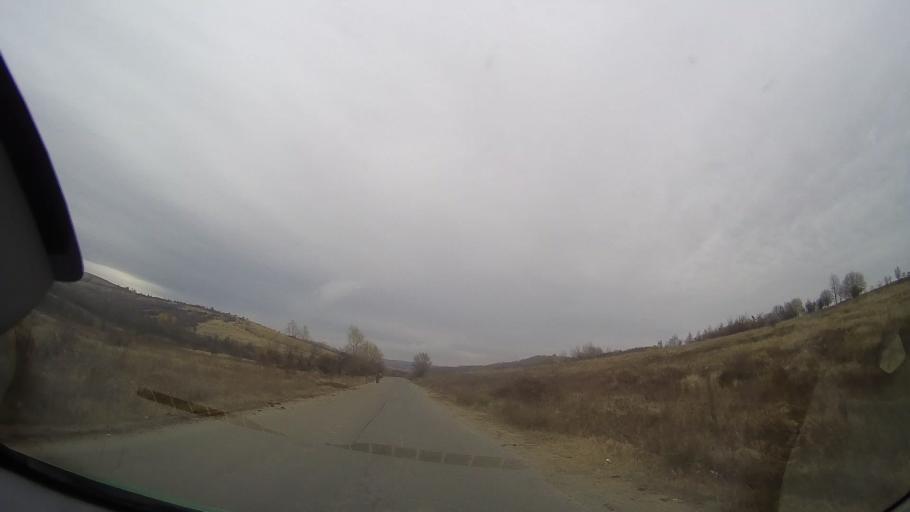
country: RO
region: Prahova
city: Mocesti
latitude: 45.0613
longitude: 26.2676
